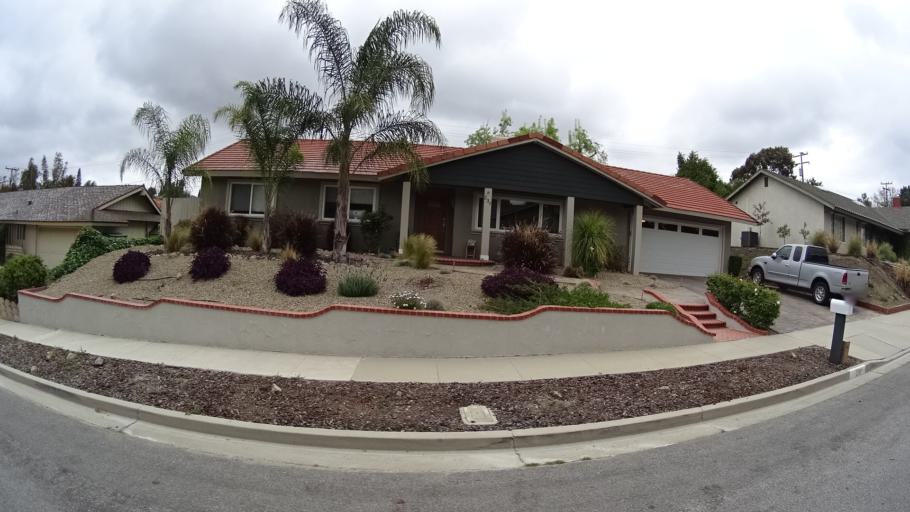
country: US
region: California
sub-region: Ventura County
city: Thousand Oaks
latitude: 34.2100
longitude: -118.8812
